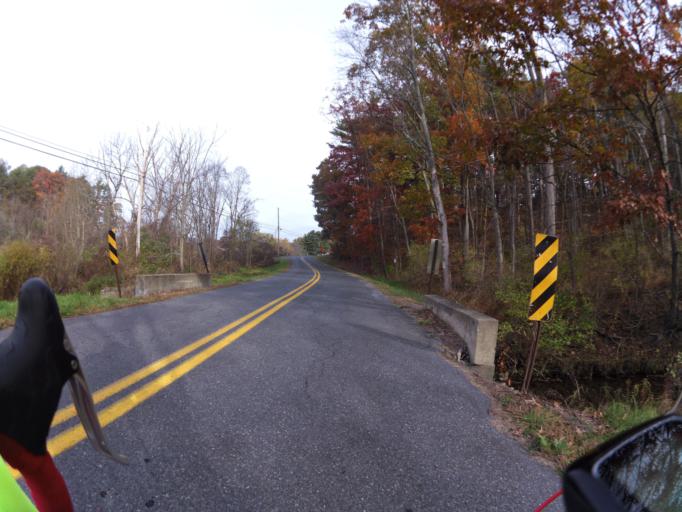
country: US
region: Pennsylvania
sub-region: Union County
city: New Columbia
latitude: 41.0406
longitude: -76.9221
